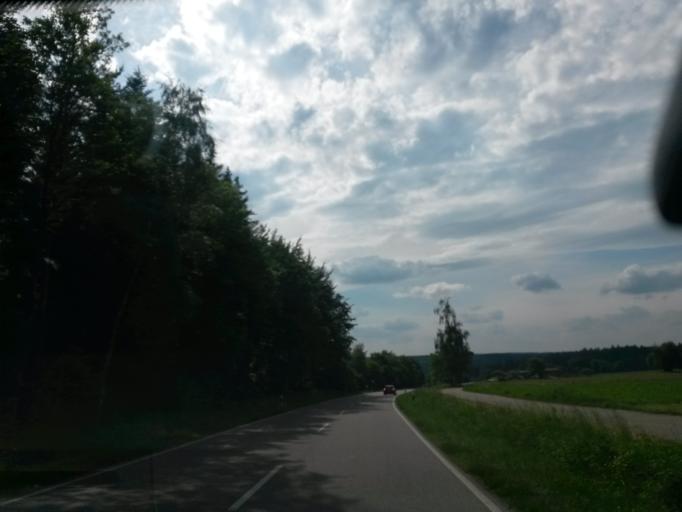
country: DE
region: Baden-Wuerttemberg
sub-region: Karlsruhe Region
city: Calw
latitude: 48.7440
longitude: 8.7591
